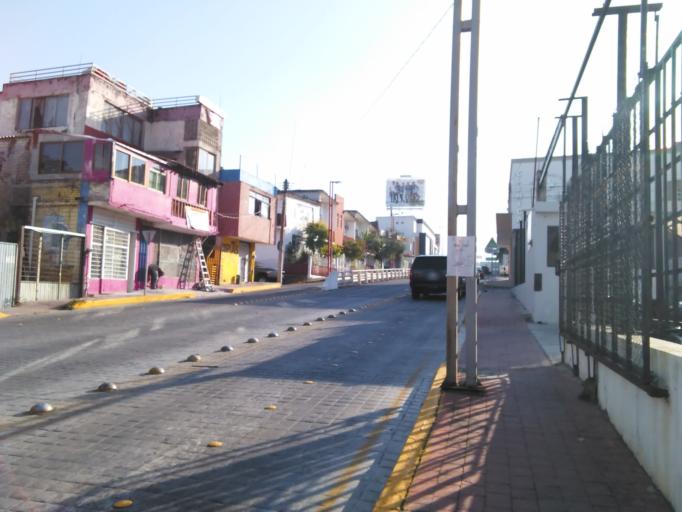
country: MX
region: Nayarit
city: Tepic
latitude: 21.5001
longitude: -104.8967
